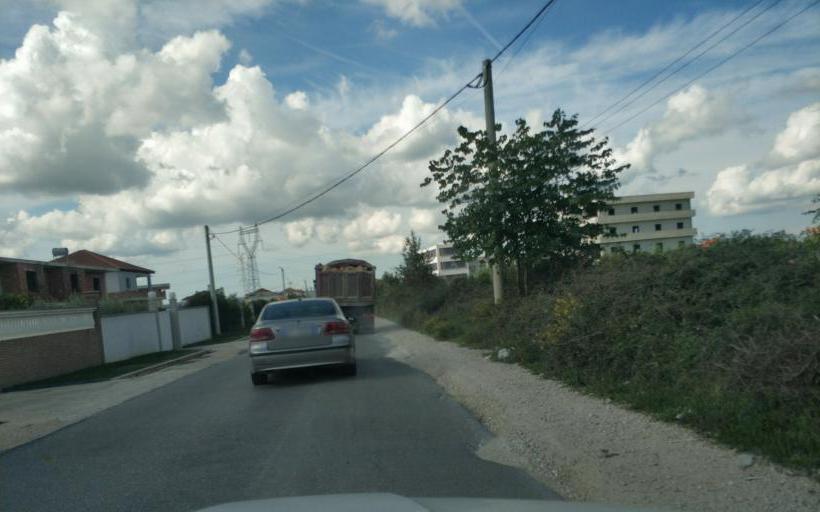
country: AL
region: Durres
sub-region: Rrethi i Krujes
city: Fushe-Kruje
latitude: 41.4766
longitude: 19.7460
